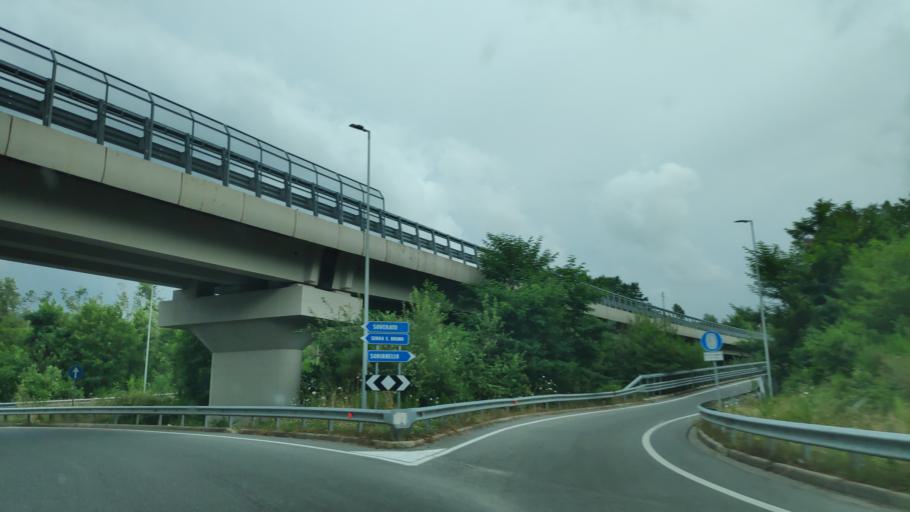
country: IT
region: Calabria
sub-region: Provincia di Vibo-Valentia
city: Spadola
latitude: 38.5924
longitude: 16.3308
